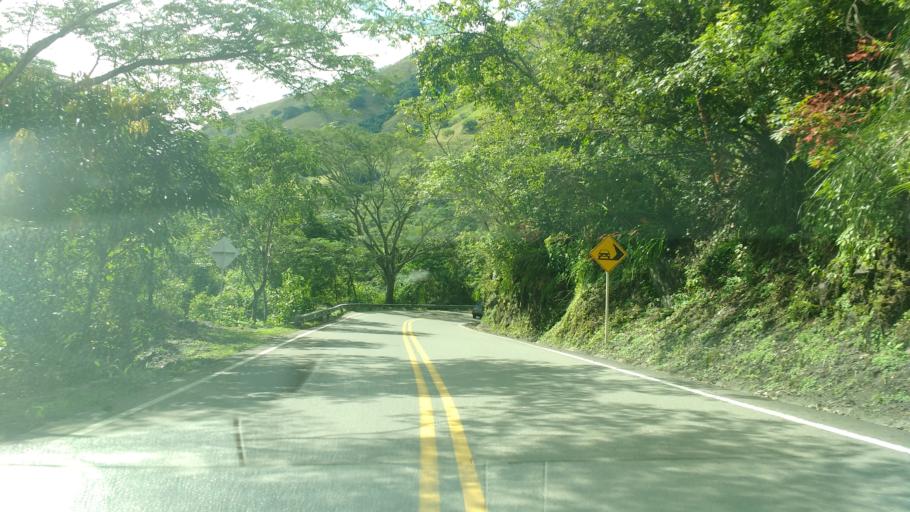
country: CO
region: Antioquia
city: Titiribi
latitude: 6.0039
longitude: -75.7944
